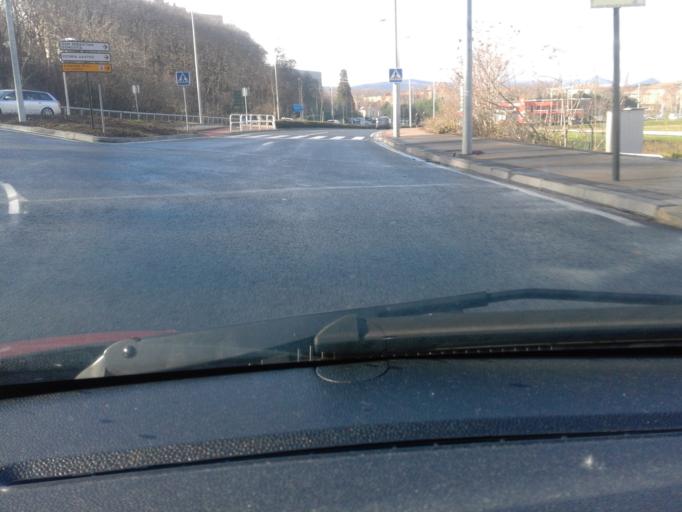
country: ES
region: Navarre
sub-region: Provincia de Navarra
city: Primer Ensanche
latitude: 42.8199
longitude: -1.6530
